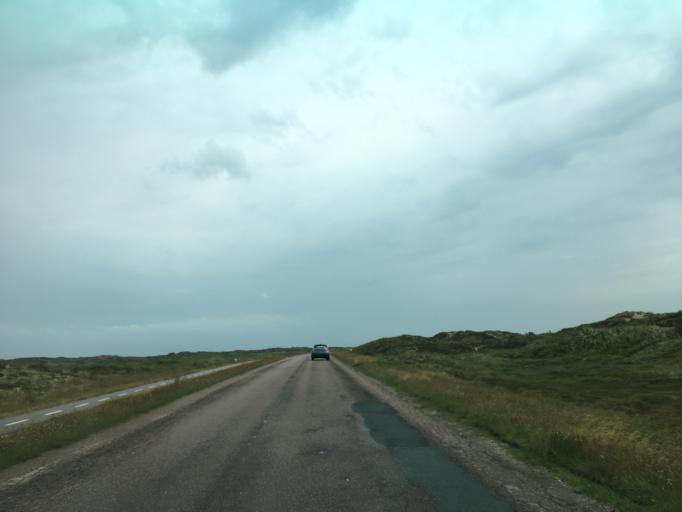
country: DK
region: North Denmark
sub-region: Thisted Kommune
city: Hurup
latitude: 56.9579
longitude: 8.3817
